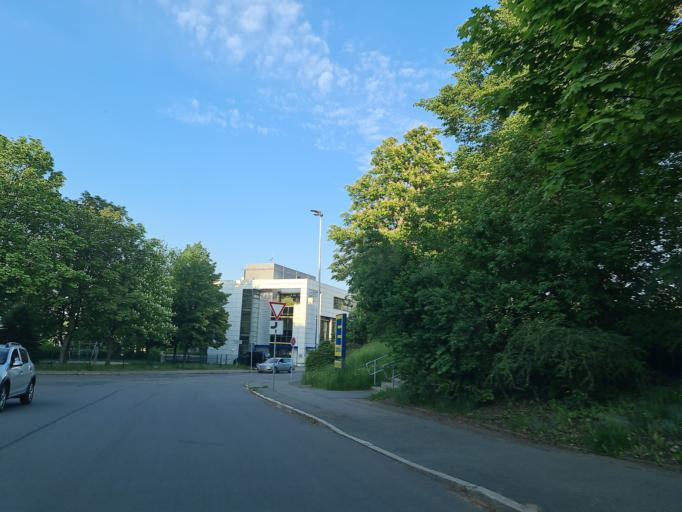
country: DE
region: Saxony
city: Chemnitz
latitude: 50.8144
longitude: 12.8967
